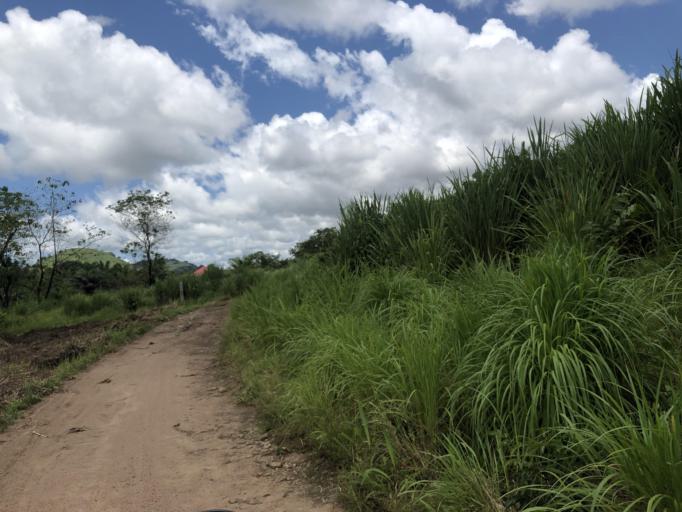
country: SL
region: Northern Province
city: Makeni
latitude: 8.8526
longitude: -12.0625
